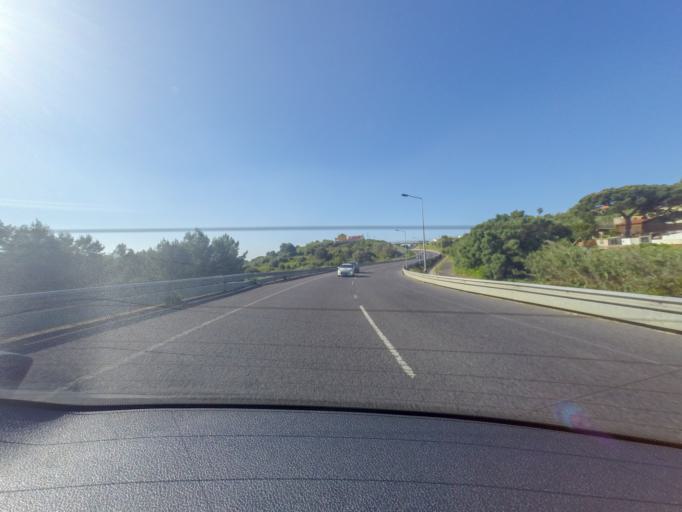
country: PT
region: Lisbon
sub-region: Cascais
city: Alcabideche
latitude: 38.7207
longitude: -9.4168
